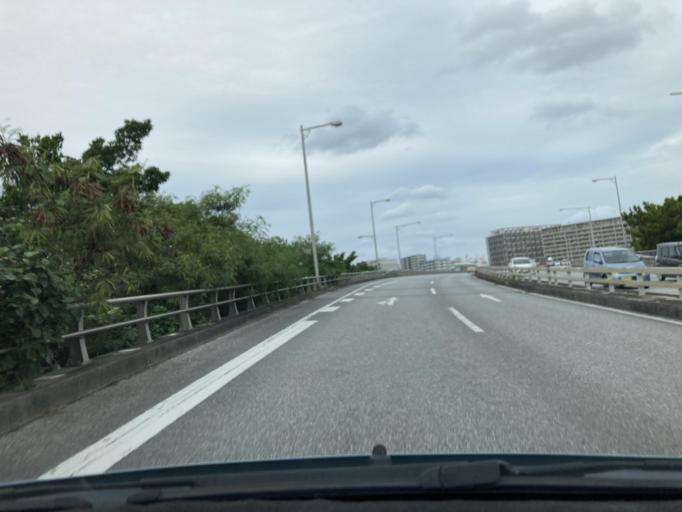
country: JP
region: Okinawa
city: Tomigusuku
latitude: 26.1983
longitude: 127.6795
